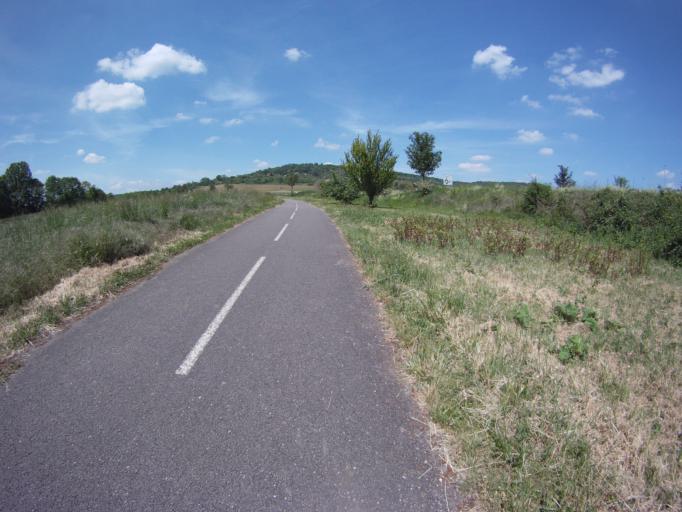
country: FR
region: Lorraine
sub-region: Departement de Meurthe-et-Moselle
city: Eulmont
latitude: 48.7419
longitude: 6.2215
